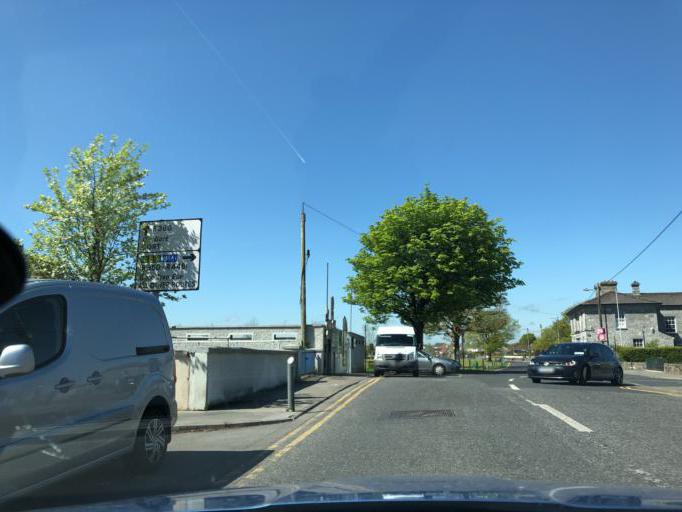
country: IE
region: Connaught
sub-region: County Galway
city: Loughrea
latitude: 53.1978
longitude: -8.5740
